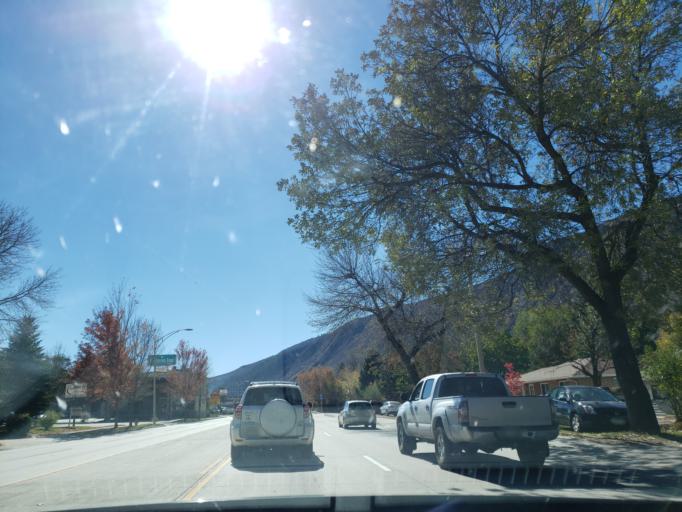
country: US
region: Colorado
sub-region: Garfield County
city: Glenwood Springs
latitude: 39.5342
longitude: -107.3253
